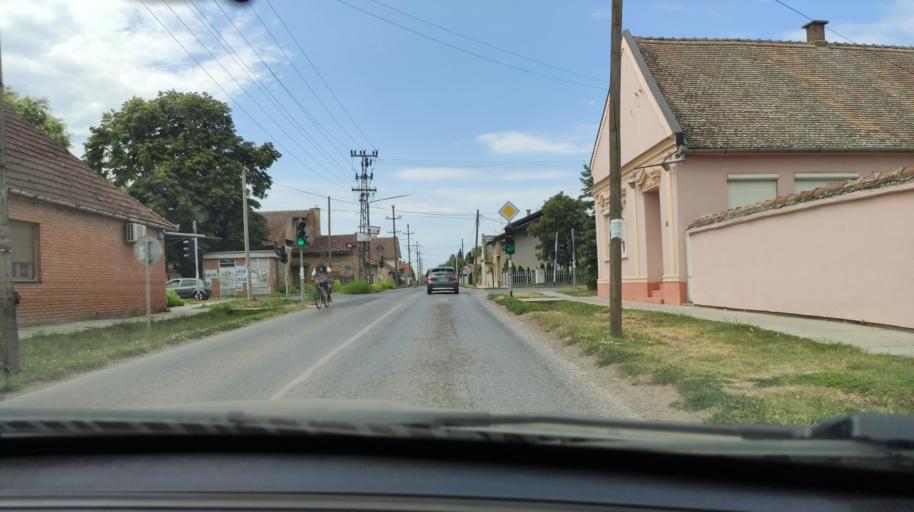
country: RS
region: Autonomna Pokrajina Vojvodina
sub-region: Juznobacki Okrug
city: Temerin
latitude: 45.4149
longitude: 19.8962
